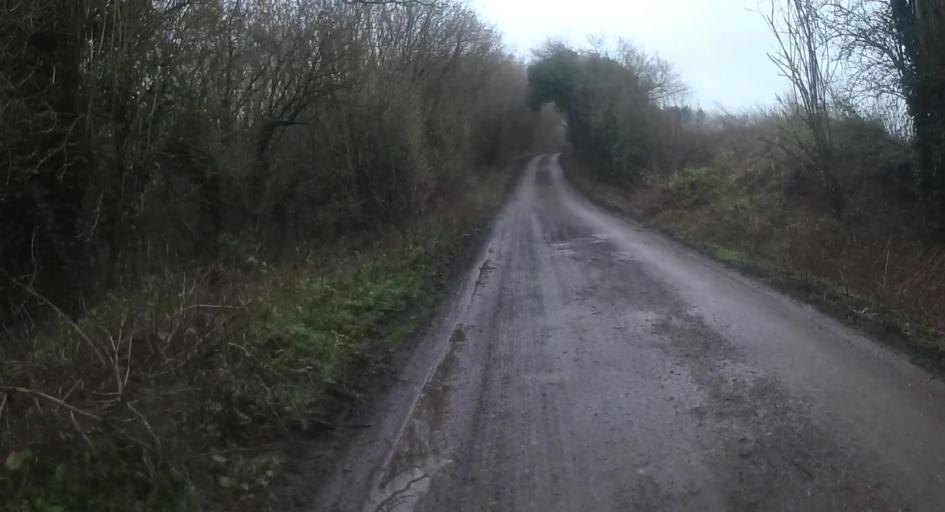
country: GB
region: England
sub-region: Hampshire
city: Kings Worthy
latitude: 51.1112
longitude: -1.2525
